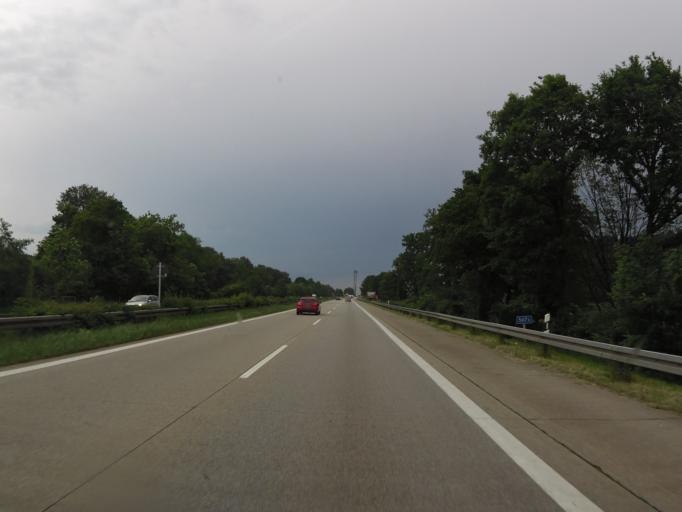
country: DE
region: Bavaria
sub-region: Lower Bavaria
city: Niederalteich
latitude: 48.7990
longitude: 12.9893
